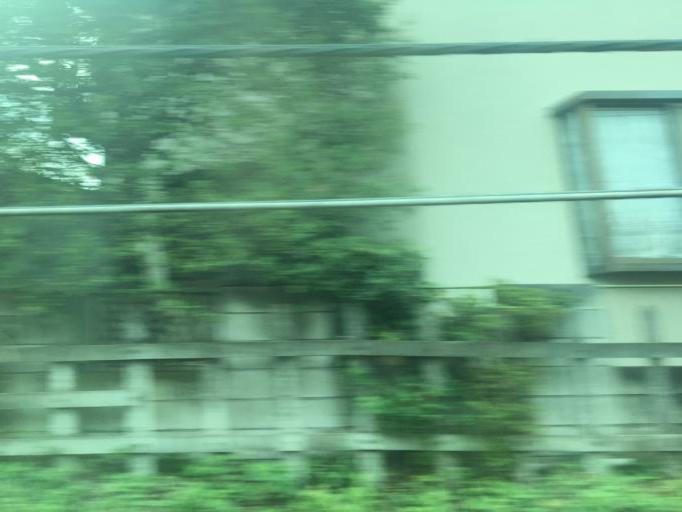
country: JP
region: Tokyo
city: Hino
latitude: 35.6891
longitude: 139.4257
